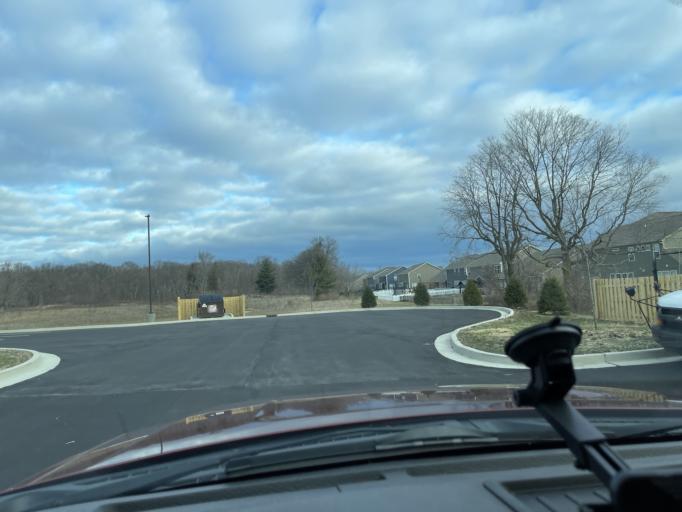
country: US
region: Indiana
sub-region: Hendricks County
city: Avon
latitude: 39.7632
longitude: -86.4575
